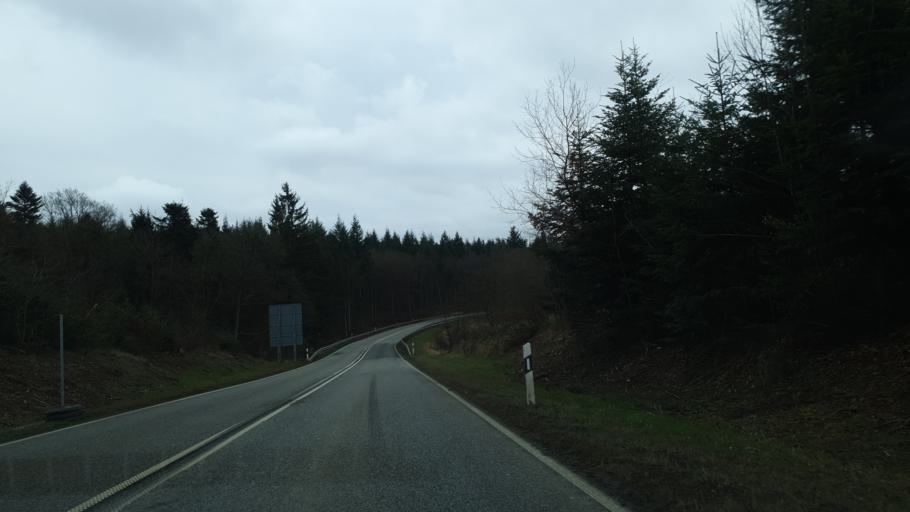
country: DE
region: Rheinland-Pfalz
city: Kratzenburg
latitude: 50.1972
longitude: 7.5758
